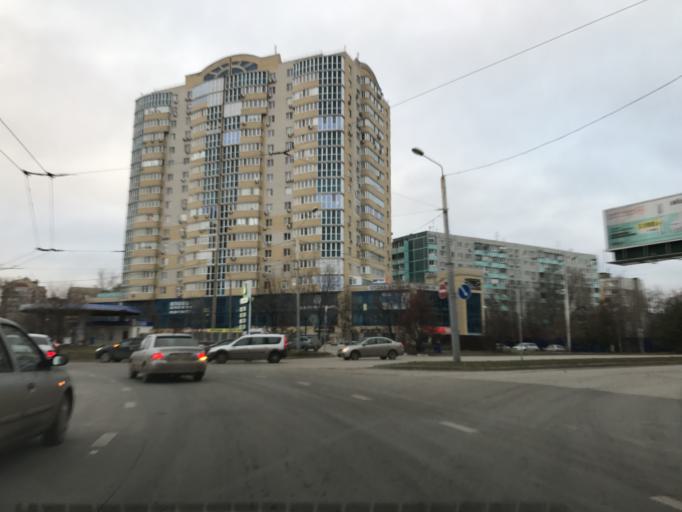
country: RU
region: Rostov
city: Severnyy
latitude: 47.2957
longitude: 39.7136
